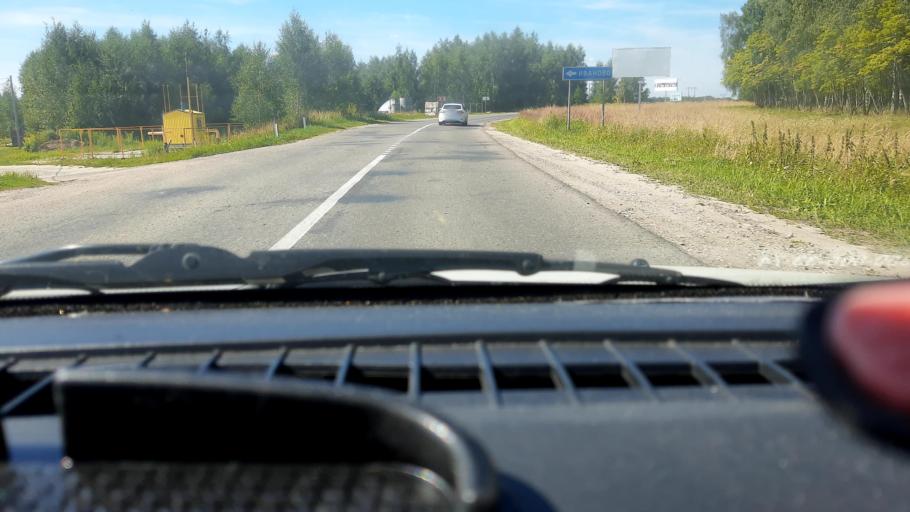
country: RU
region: Nizjnij Novgorod
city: Zavolzh'ye
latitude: 56.6922
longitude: 43.4190
